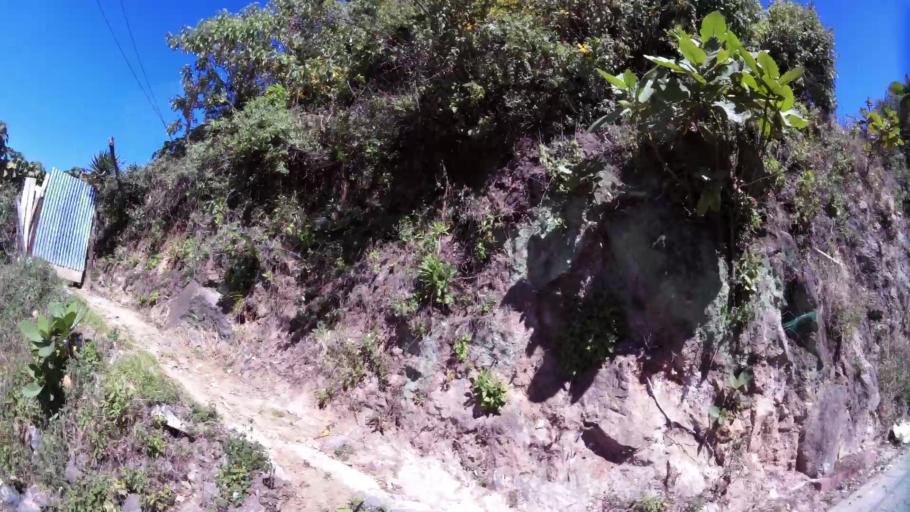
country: GT
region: Solola
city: Solola
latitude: 14.7729
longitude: -91.1850
